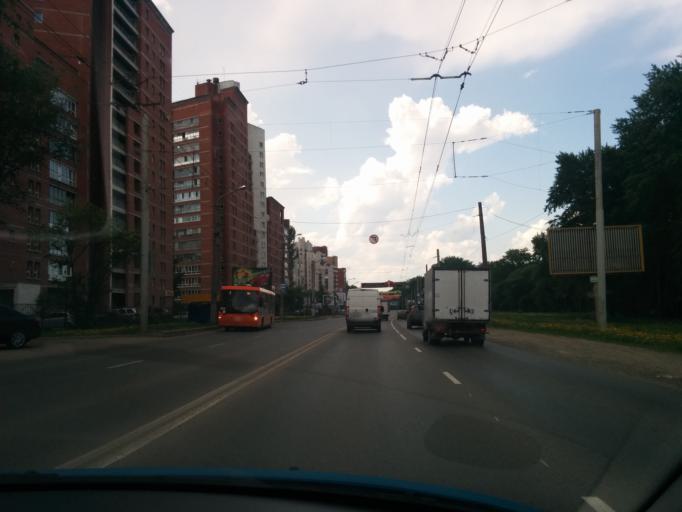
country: RU
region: Perm
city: Kondratovo
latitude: 57.9802
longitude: 56.1755
